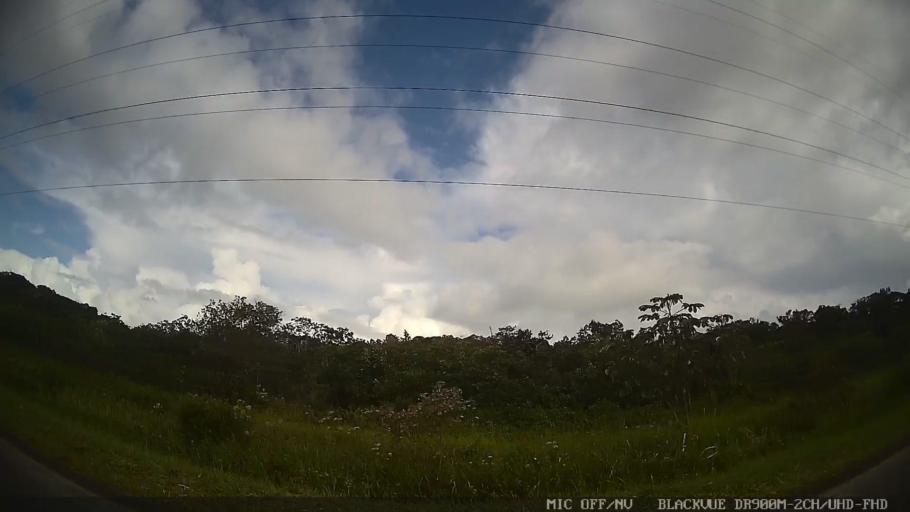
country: BR
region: Sao Paulo
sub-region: Peruibe
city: Peruibe
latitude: -24.2533
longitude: -46.9335
